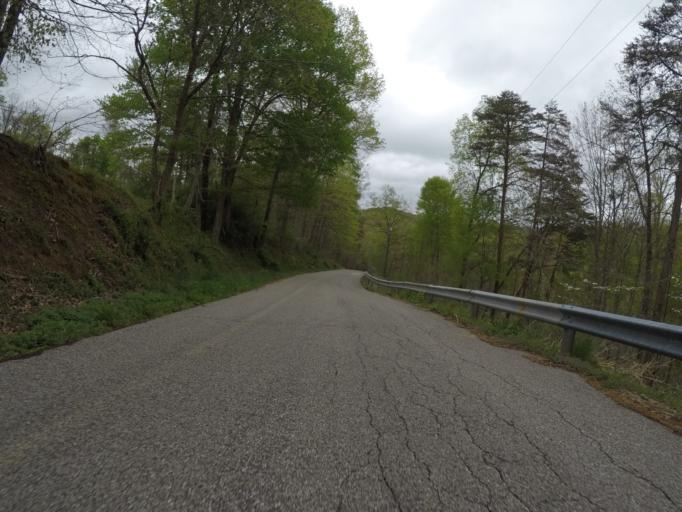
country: US
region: West Virginia
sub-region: Cabell County
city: Barboursville
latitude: 38.3891
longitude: -82.2503
